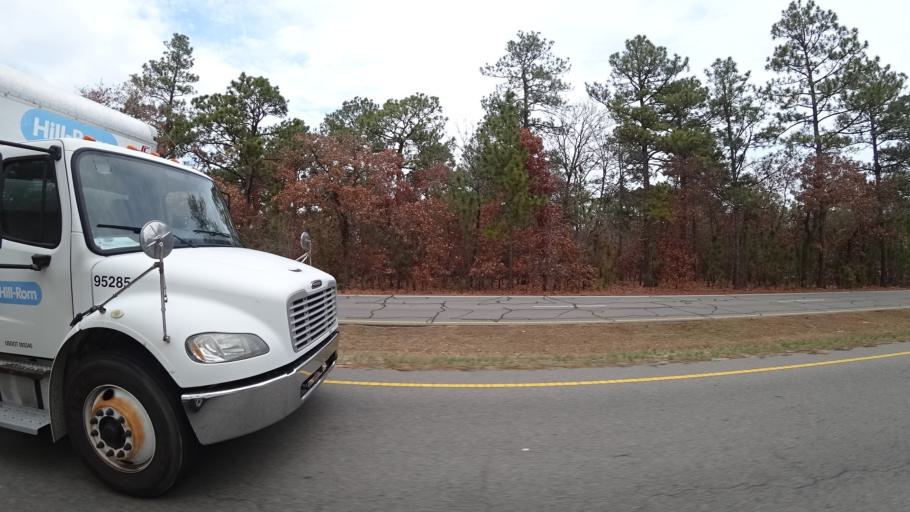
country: US
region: North Carolina
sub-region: Moore County
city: Pinehurst
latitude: 35.2030
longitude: -79.4451
